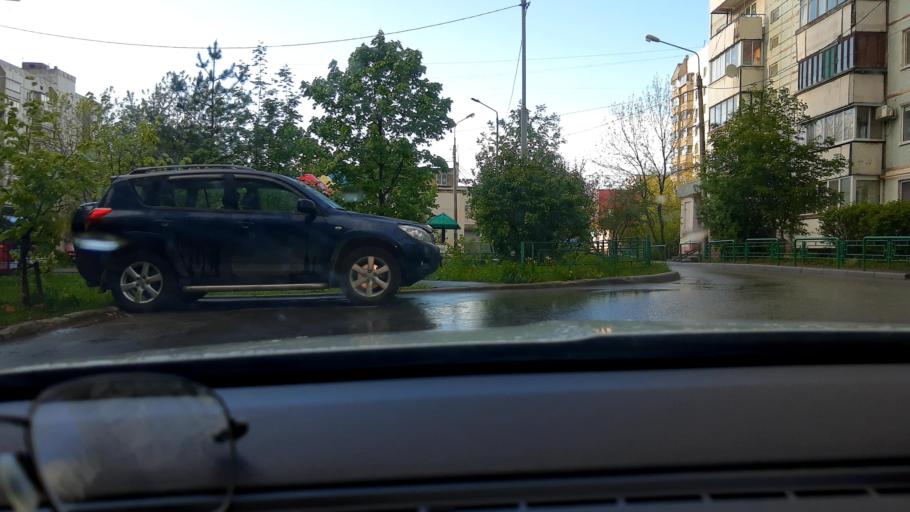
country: RU
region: Moskovskaya
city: Nakhabino
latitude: 55.8390
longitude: 37.1761
